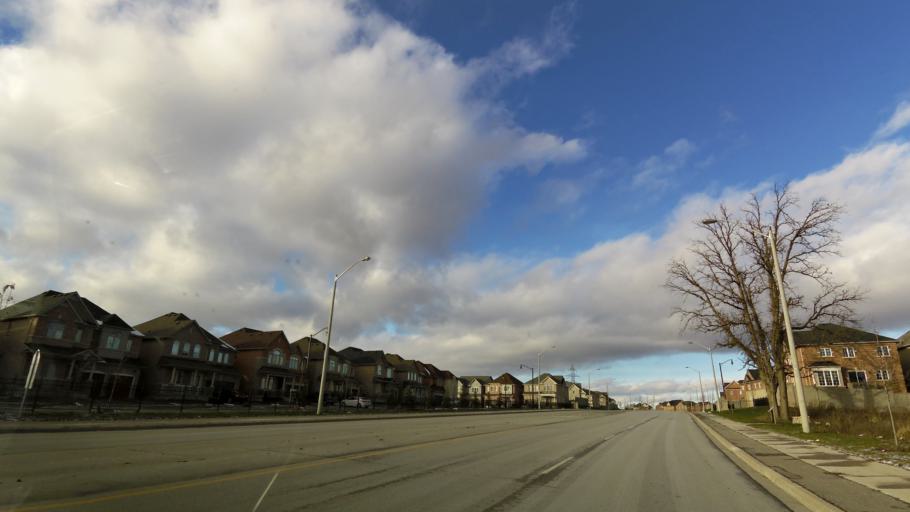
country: CA
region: Ontario
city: Brampton
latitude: 43.6578
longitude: -79.7824
